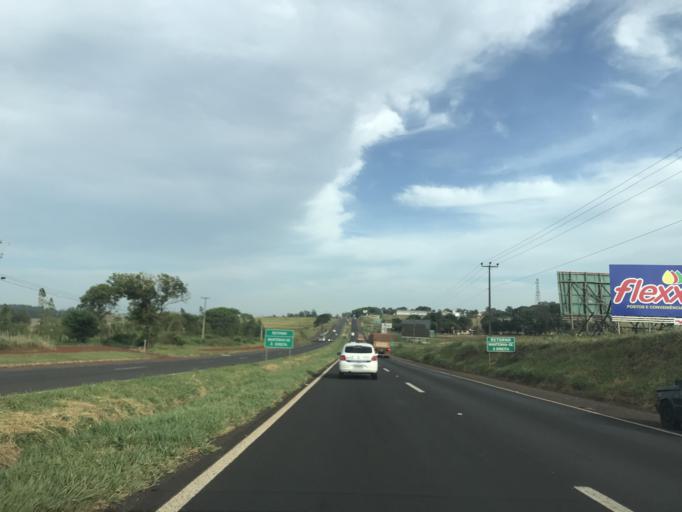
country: BR
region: Parana
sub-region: Maringa
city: Maringa
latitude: -23.3967
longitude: -52.0051
